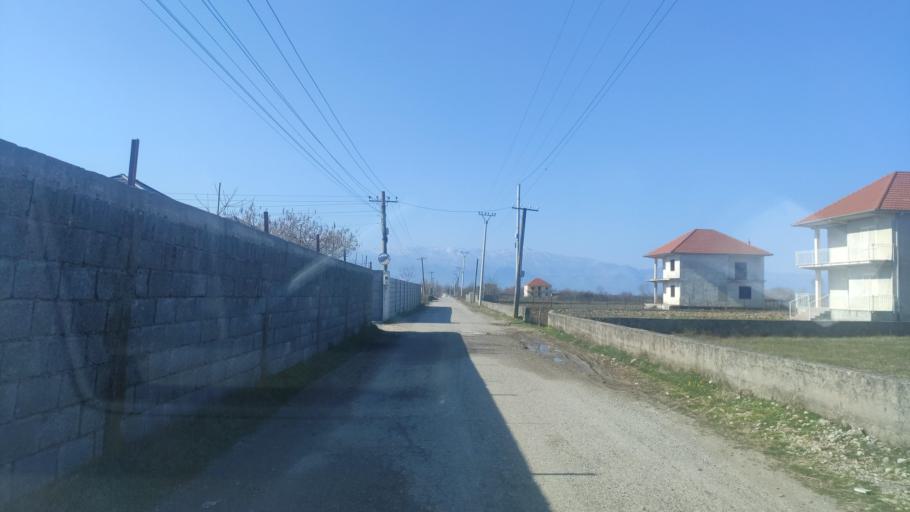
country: AL
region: Shkoder
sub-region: Rrethi i Malesia e Madhe
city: Grude-Fushe
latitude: 42.1608
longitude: 19.4558
